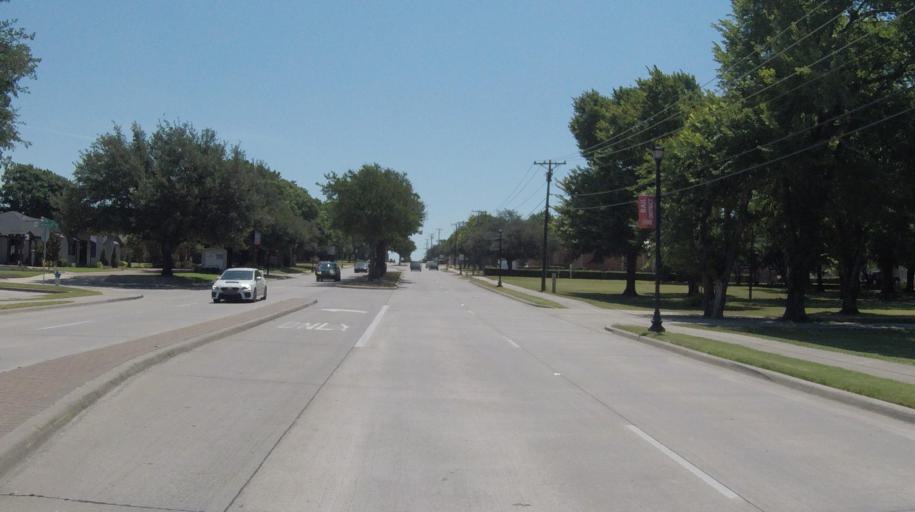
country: US
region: Texas
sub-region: Collin County
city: Frisco
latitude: 33.1498
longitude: -96.8184
